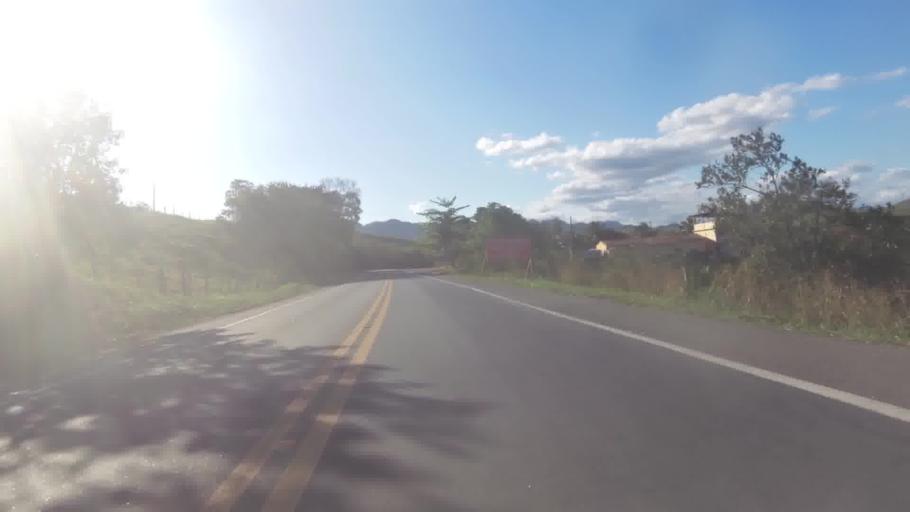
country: BR
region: Espirito Santo
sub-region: Iconha
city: Iconha
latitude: -20.7666
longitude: -40.7597
